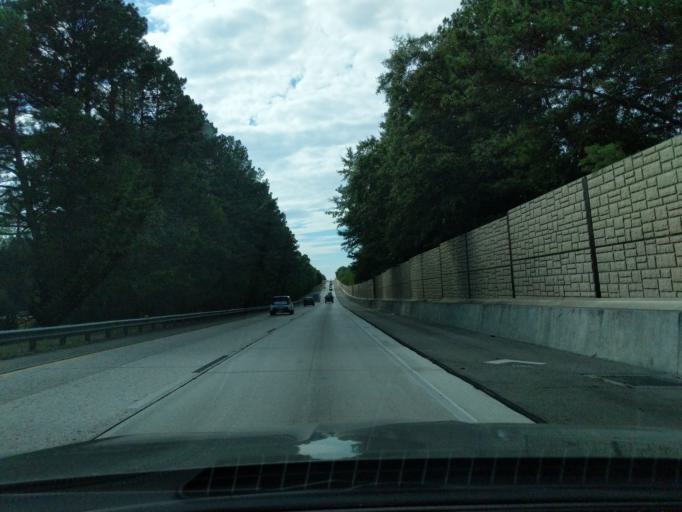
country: US
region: Georgia
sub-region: Columbia County
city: Grovetown
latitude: 33.4791
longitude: -82.1503
